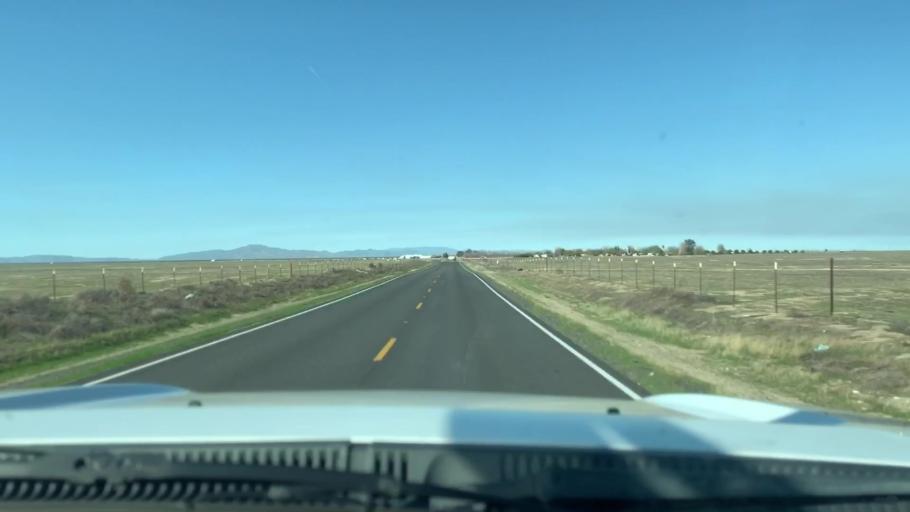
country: US
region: California
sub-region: Kern County
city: Lost Hills
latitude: 35.6029
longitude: -119.8530
